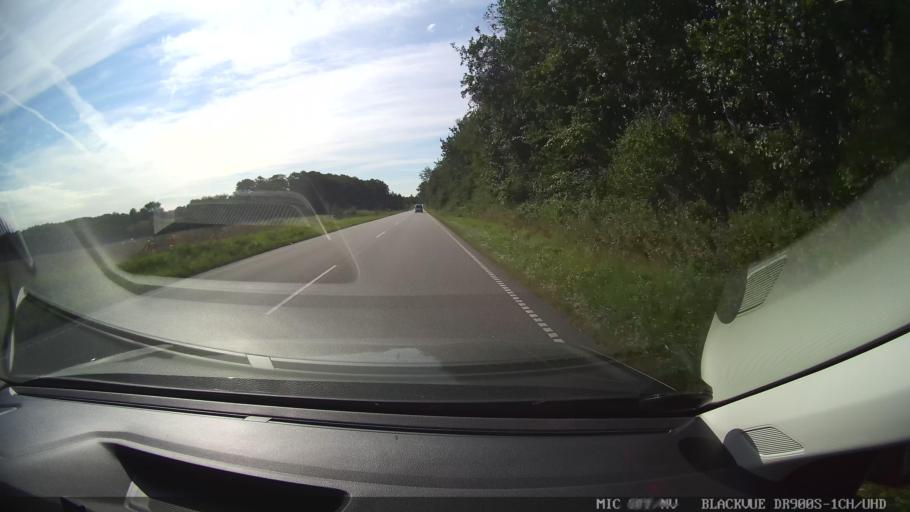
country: DK
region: North Denmark
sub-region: Mariagerfjord Kommune
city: Hadsund
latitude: 56.7428
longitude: 10.0760
